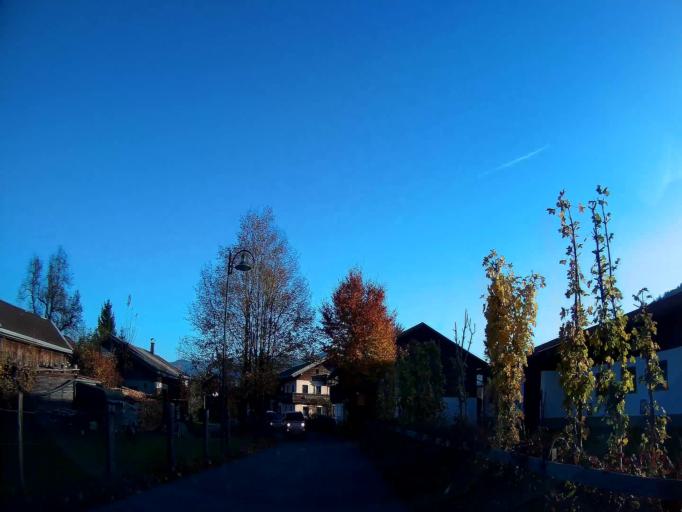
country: AT
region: Salzburg
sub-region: Politischer Bezirk Zell am See
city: Saalfelden am Steinernen Meer
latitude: 47.4462
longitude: 12.8163
